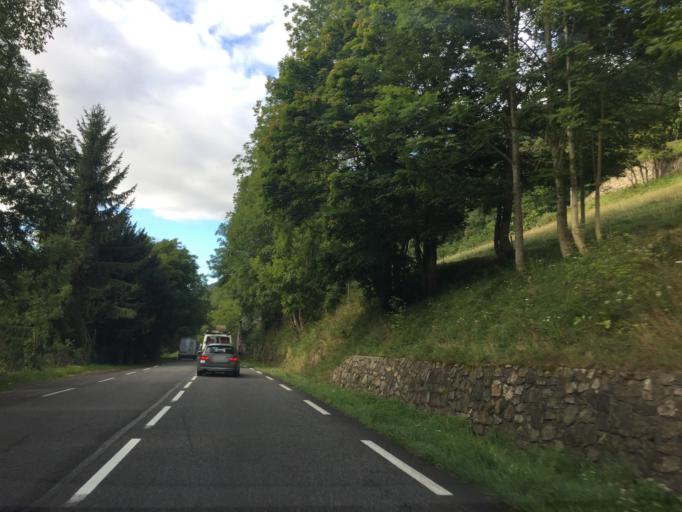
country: FR
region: Midi-Pyrenees
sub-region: Departement des Hautes-Pyrenees
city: La Barthe-de-Neste
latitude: 42.9850
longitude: 0.3759
